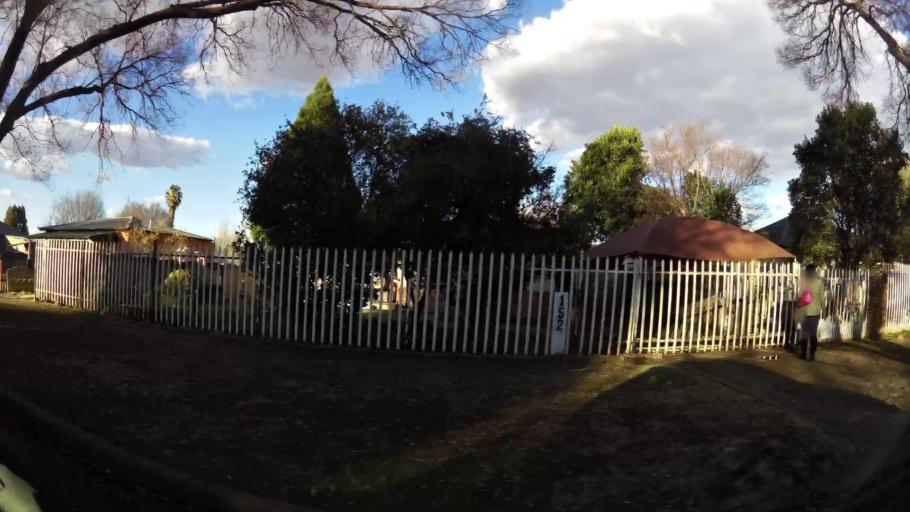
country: ZA
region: North-West
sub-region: Dr Kenneth Kaunda District Municipality
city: Potchefstroom
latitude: -26.7219
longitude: 27.1005
